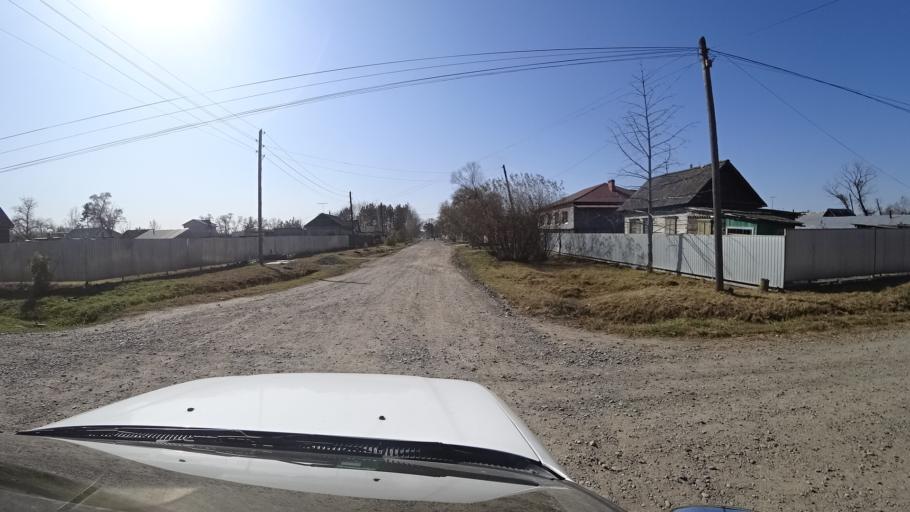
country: RU
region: Primorskiy
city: Dal'nerechensk
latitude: 45.9264
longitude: 133.7427
